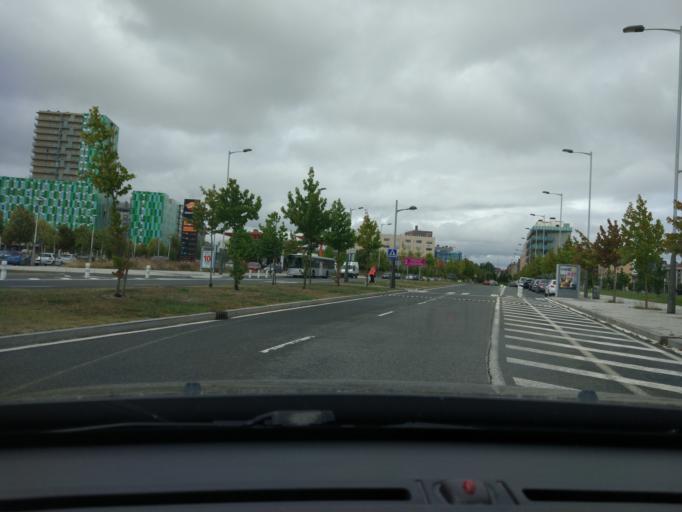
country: ES
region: Basque Country
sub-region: Provincia de Alava
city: Gasteiz / Vitoria
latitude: 42.8498
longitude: -2.6465
